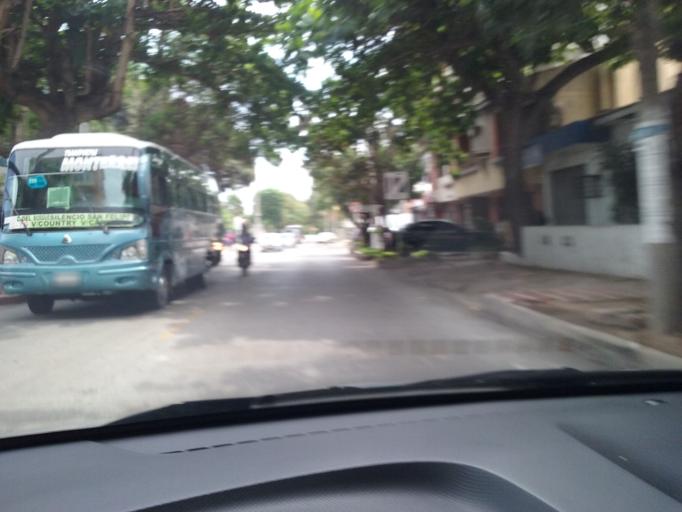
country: CO
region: Atlantico
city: Barranquilla
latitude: 11.0115
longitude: -74.8080
